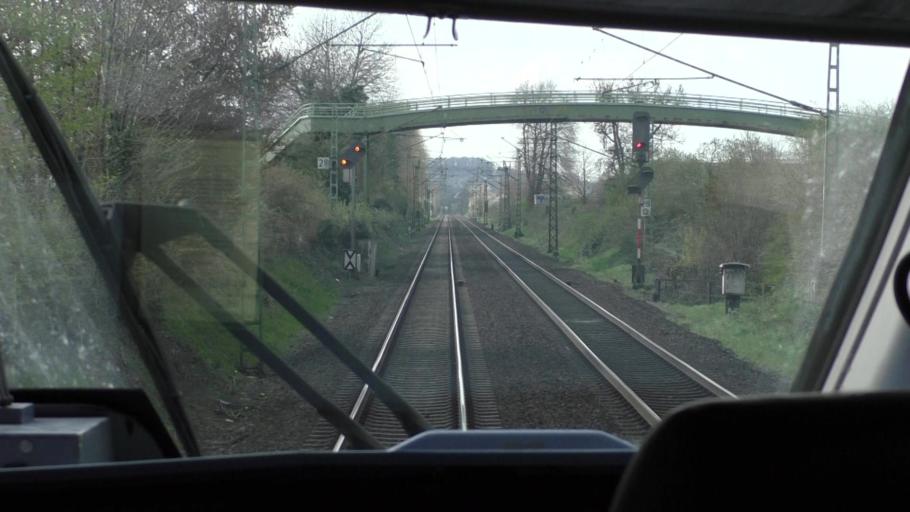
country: DE
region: North Rhine-Westphalia
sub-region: Regierungsbezirk Koln
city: Alfter
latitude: 50.7442
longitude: 7.0466
